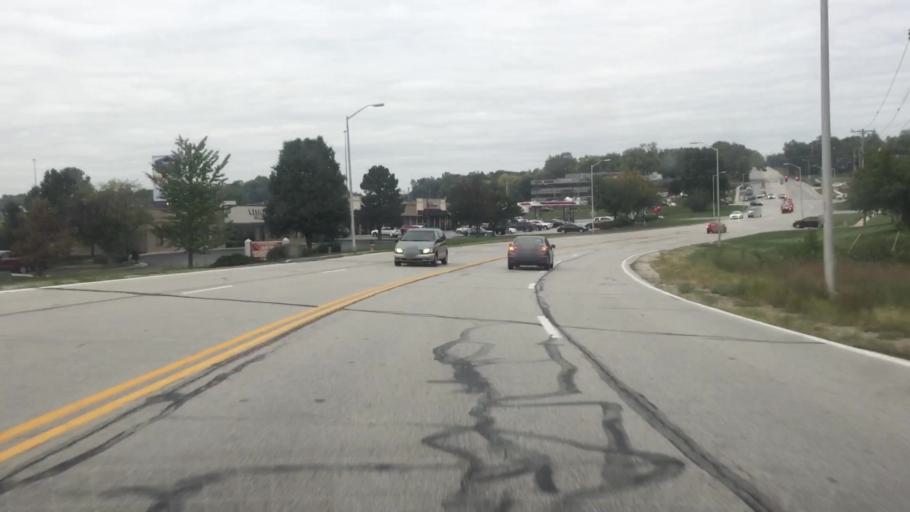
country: US
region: Kansas
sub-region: Johnson County
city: Lenexa
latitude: 38.9970
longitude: -94.7800
